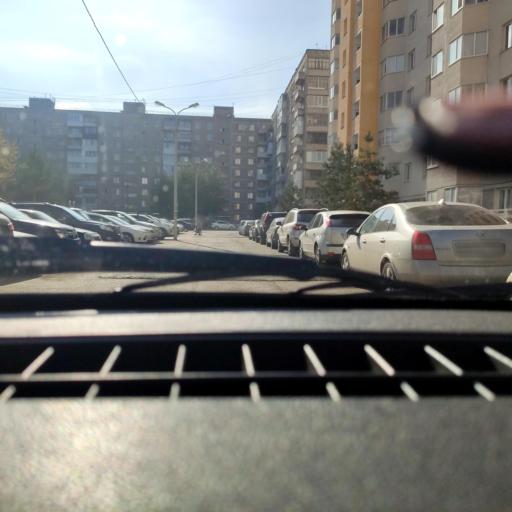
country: RU
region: Bashkortostan
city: Ufa
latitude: 54.7775
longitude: 56.1197
